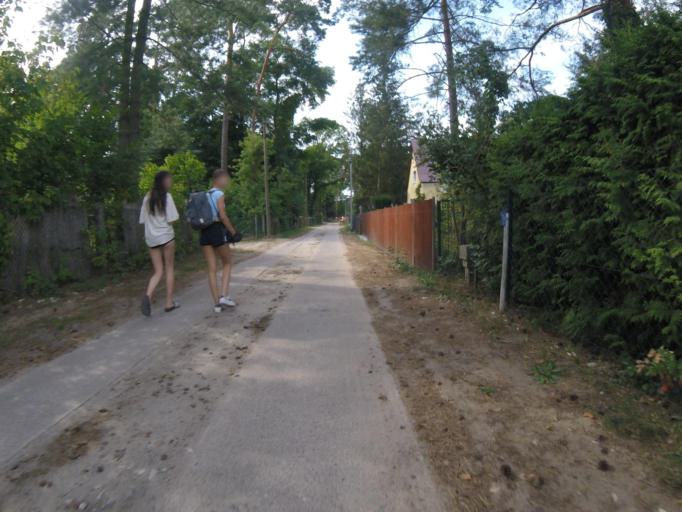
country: DE
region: Brandenburg
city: Wildau
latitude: 52.3148
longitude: 13.7159
